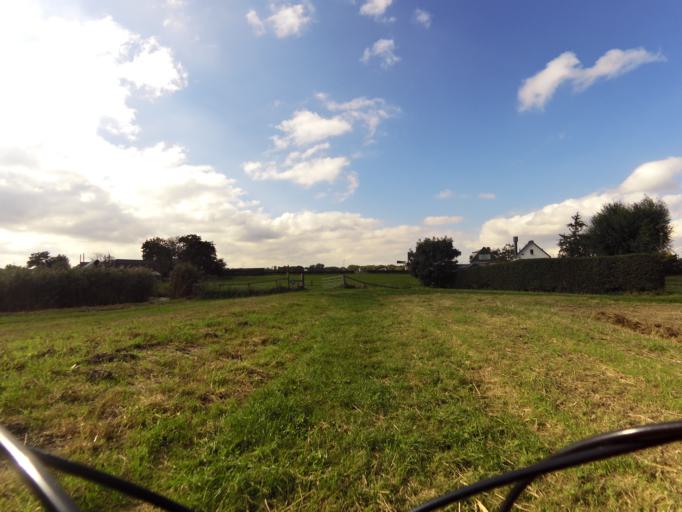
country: NL
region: South Holland
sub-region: Gemeente Voorschoten
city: Voorschoten
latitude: 52.1049
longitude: 4.4365
